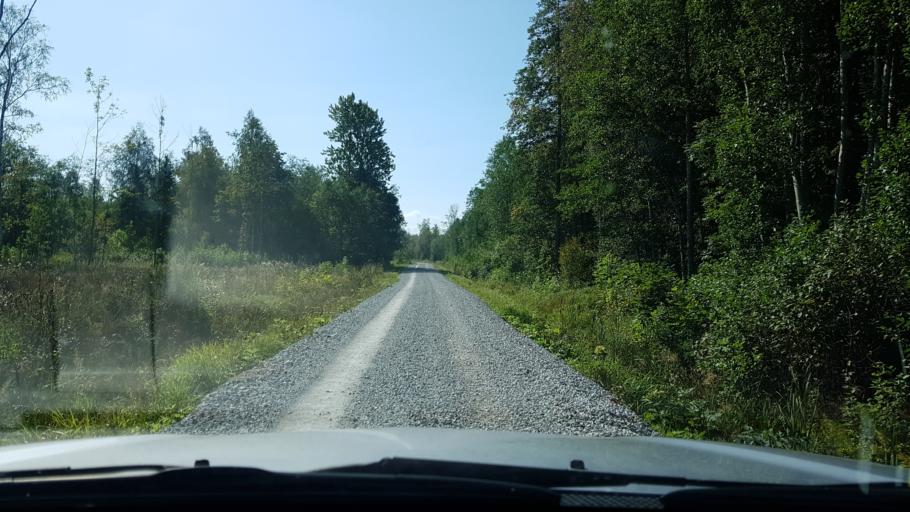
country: EE
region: Ida-Virumaa
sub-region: Sillamaee linn
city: Sillamae
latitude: 59.3386
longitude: 27.7337
